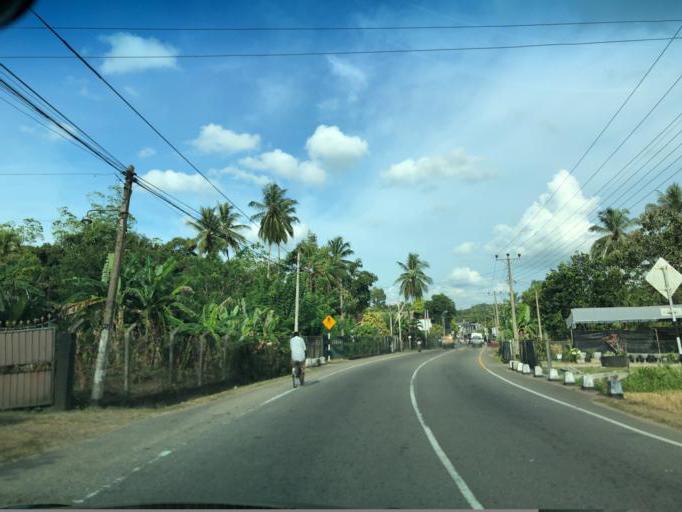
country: LK
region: Western
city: Horawala Junction
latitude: 6.5265
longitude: 80.0907
